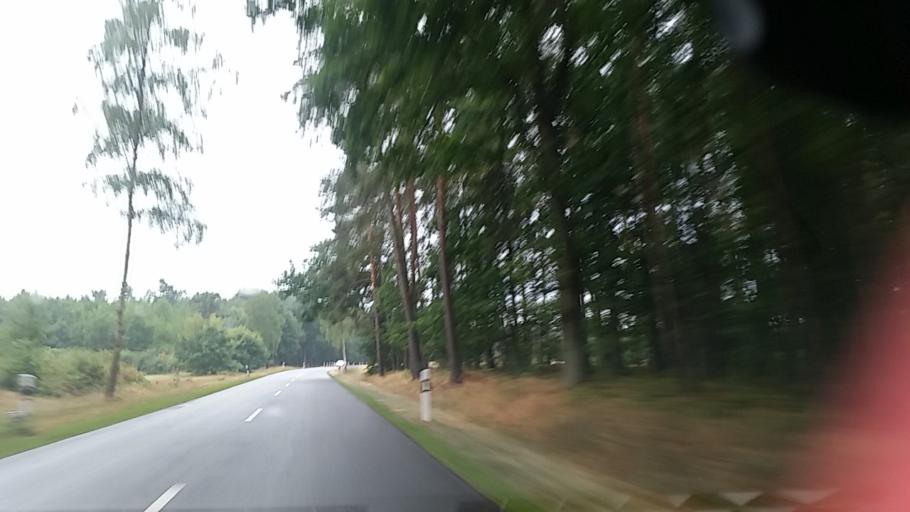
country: DE
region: Lower Saxony
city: Schoneworde
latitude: 52.6464
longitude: 10.6989
